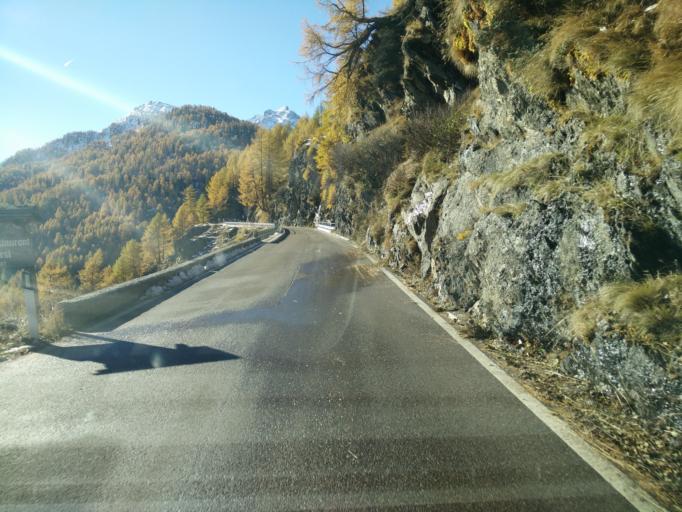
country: IT
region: Trentino-Alto Adige
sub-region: Bolzano
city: Moso in Passiria
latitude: 46.8907
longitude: 11.1273
